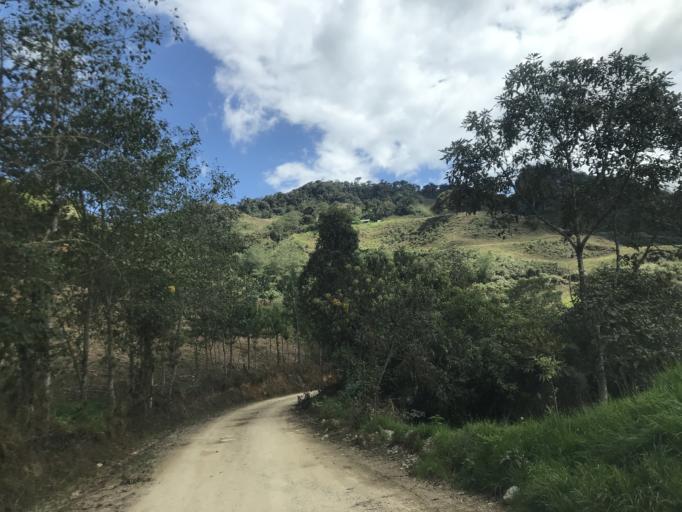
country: PE
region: Cajamarca
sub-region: Provincia de Chota
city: Querocoto
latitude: -6.3460
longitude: -79.0538
